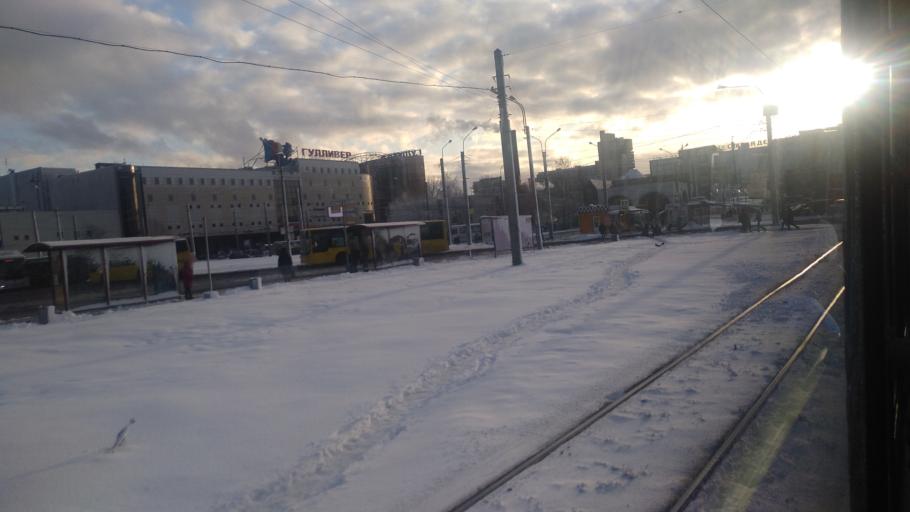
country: RU
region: St.-Petersburg
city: Staraya Derevnya
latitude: 59.9912
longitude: 30.2538
